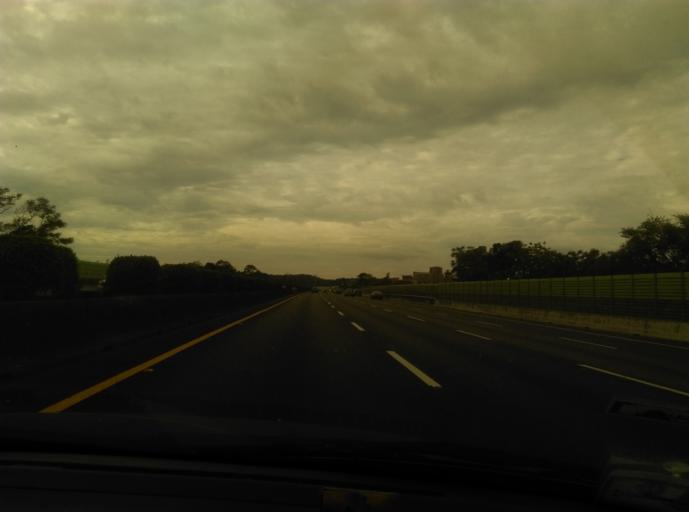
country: TW
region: Taiwan
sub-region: Taoyuan
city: Taoyuan
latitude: 24.9361
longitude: 121.3417
